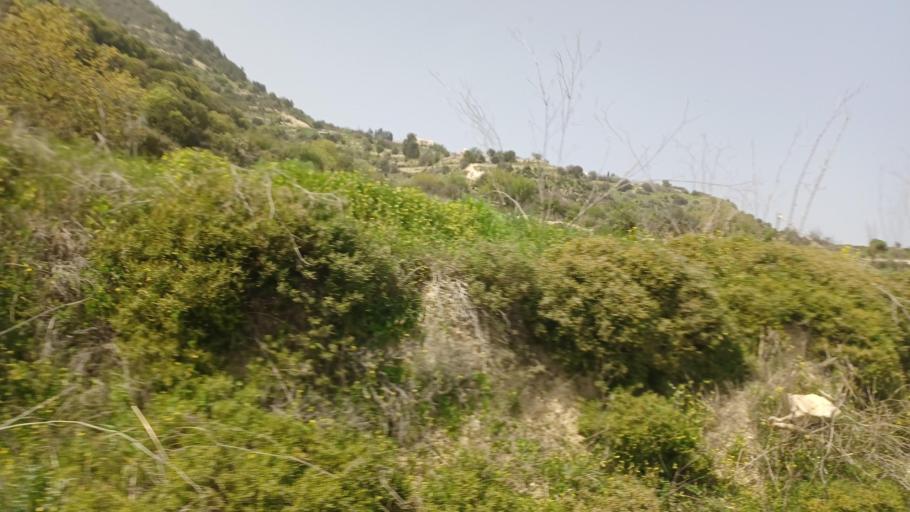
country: CY
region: Limassol
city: Pachna
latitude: 34.7769
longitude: 32.7463
